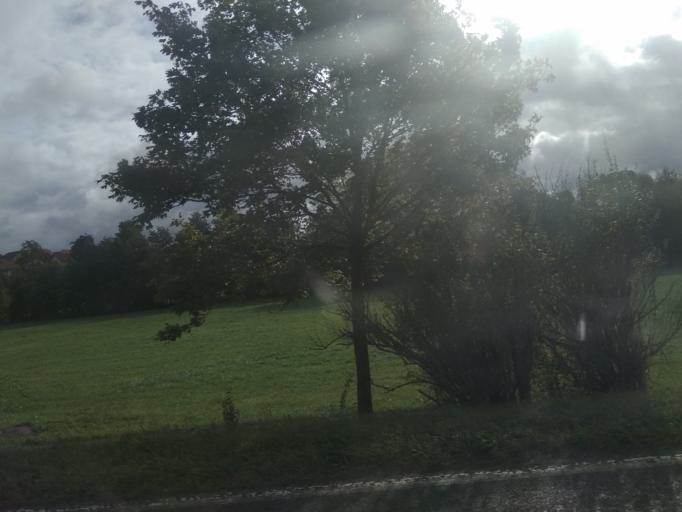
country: DE
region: Baden-Wuerttemberg
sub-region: Karlsruhe Region
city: Seckach
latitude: 49.4091
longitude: 9.2807
